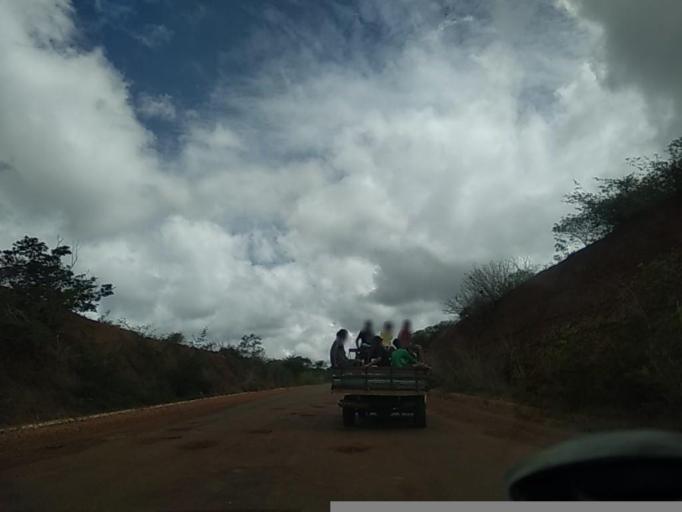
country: BR
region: Bahia
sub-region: Caetite
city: Caetite
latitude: -14.0264
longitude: -42.4884
